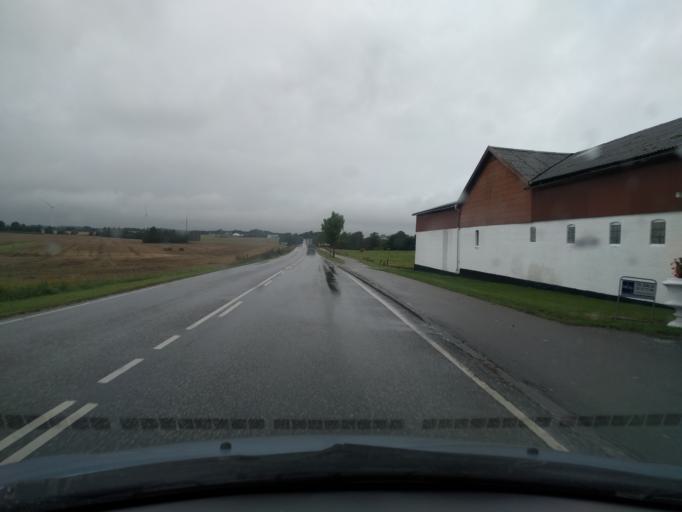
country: DK
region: Zealand
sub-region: Naestved Kommune
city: Fuglebjerg
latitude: 55.2671
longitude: 11.6492
